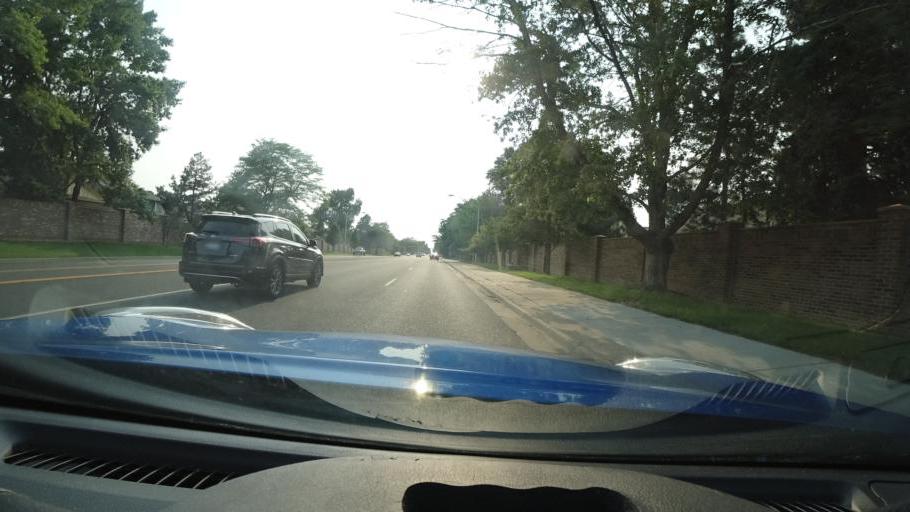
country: US
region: Colorado
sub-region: Adams County
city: Aurora
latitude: 39.6677
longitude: -104.8440
